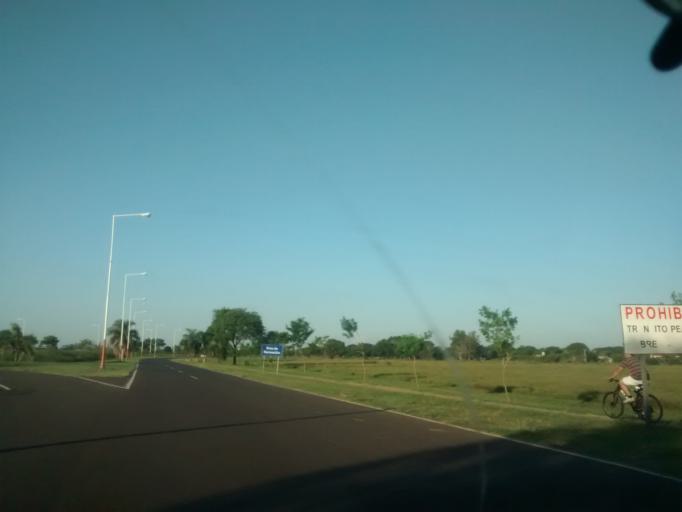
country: AR
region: Chaco
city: Fontana
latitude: -27.4445
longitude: -59.0417
